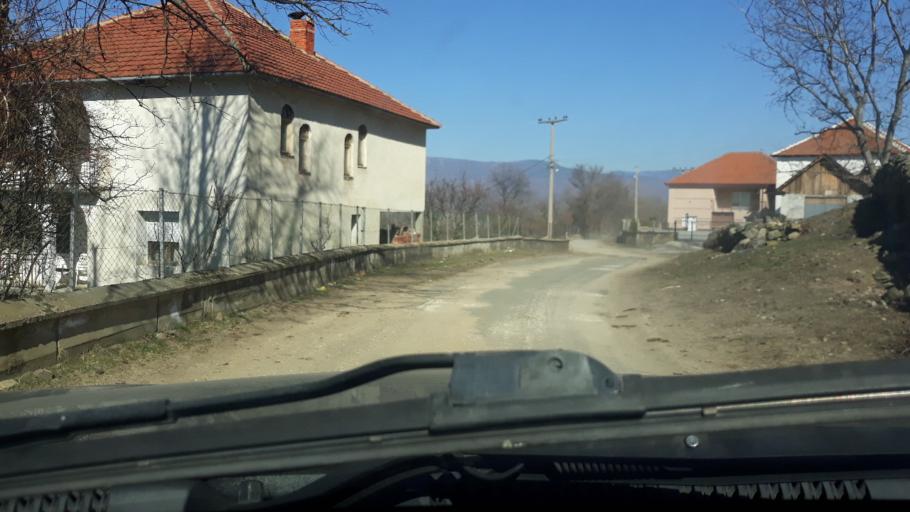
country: MK
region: Novo Selo
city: Novo Selo
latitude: 41.3764
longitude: 22.8448
